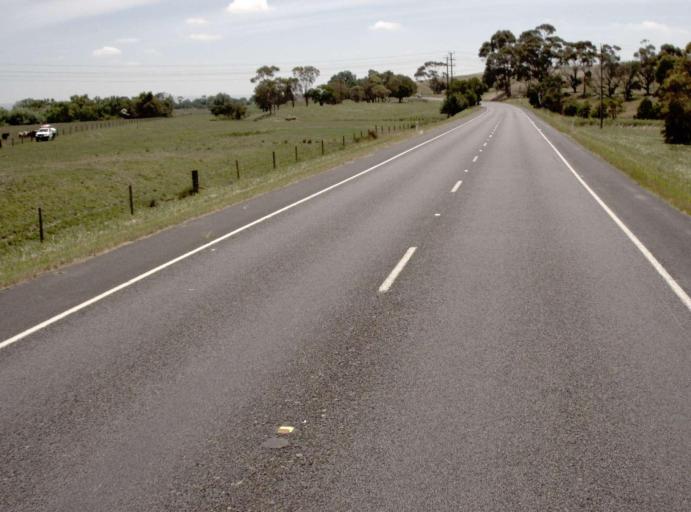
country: AU
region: Victoria
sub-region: Latrobe
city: Traralgon
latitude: -38.2224
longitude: 146.5450
